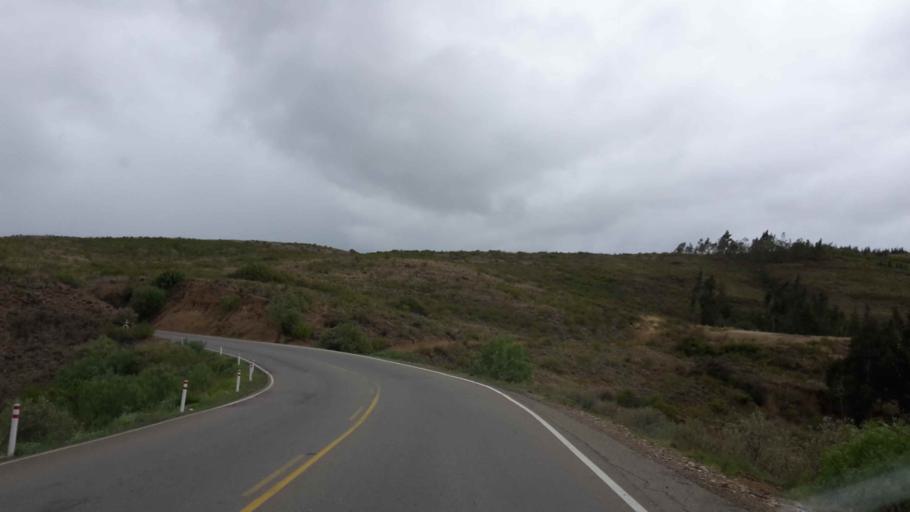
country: BO
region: Cochabamba
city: Arani
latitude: -17.4735
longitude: -65.7642
